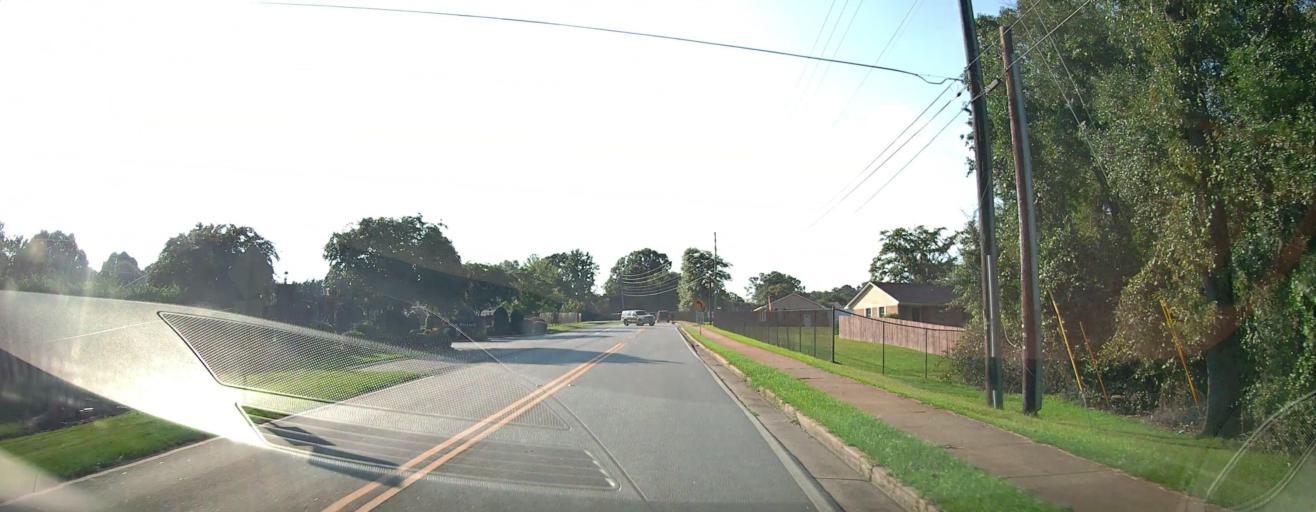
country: US
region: Georgia
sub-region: Houston County
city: Perry
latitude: 32.4688
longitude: -83.7349
